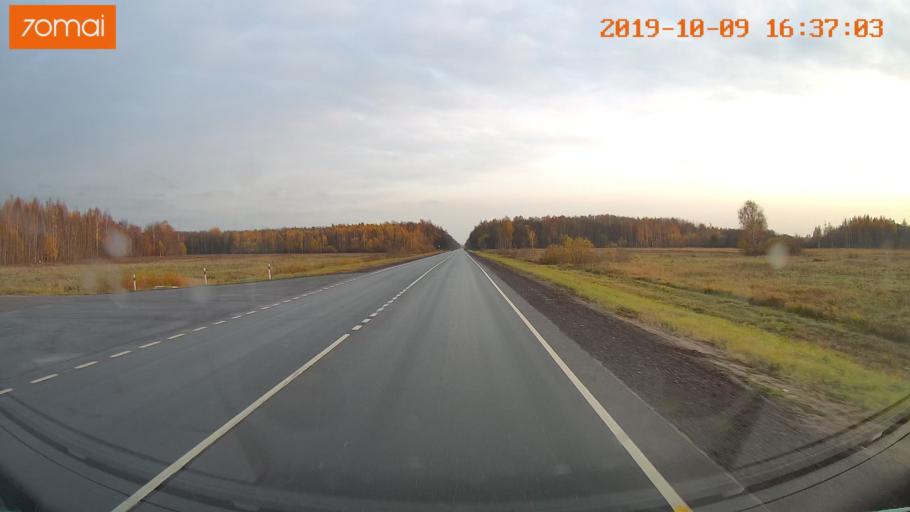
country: RU
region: Kostroma
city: Volgorechensk
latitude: 57.5327
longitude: 41.0199
